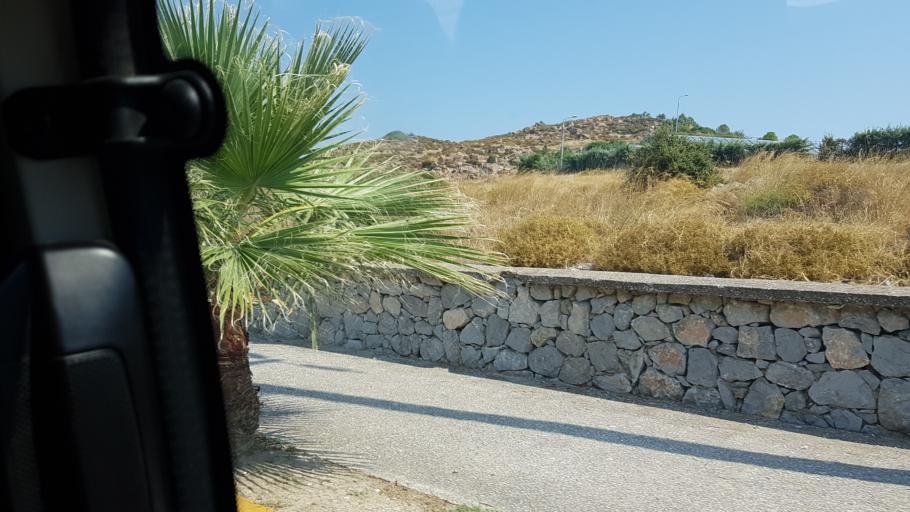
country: TR
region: Izmir
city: Urla
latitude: 38.3810
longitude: 26.7581
